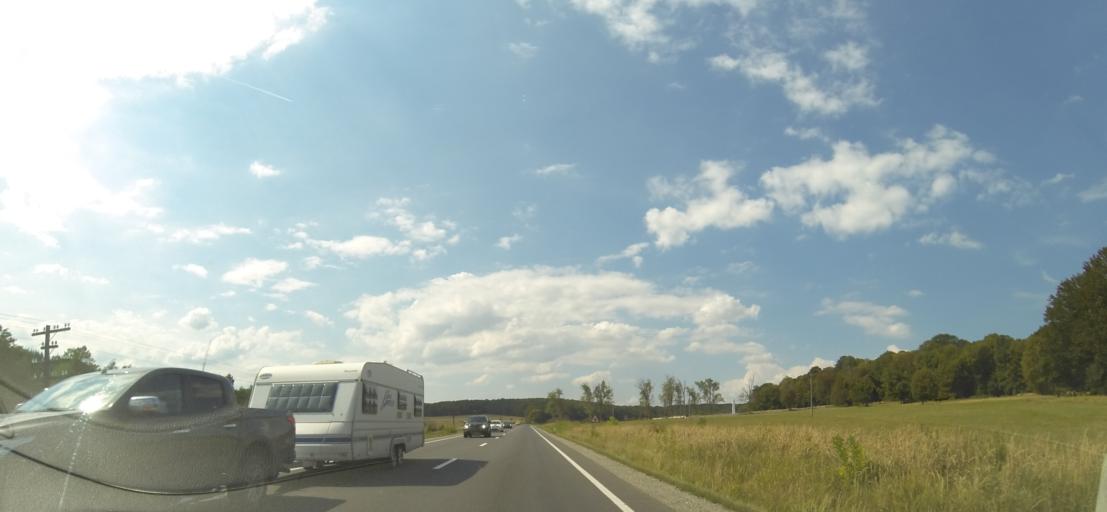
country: RO
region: Brasov
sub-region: Comuna Sinca Noua
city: Sinca Noua
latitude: 45.7447
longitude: 25.2951
